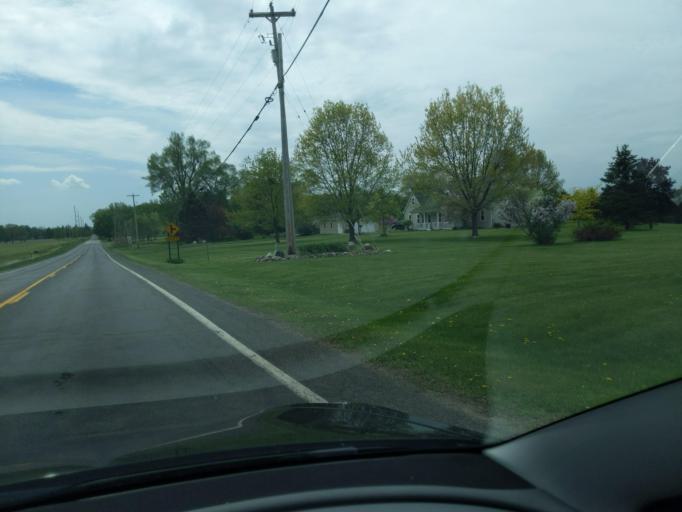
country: US
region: Michigan
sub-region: Ingham County
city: Holt
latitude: 42.6171
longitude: -84.5428
